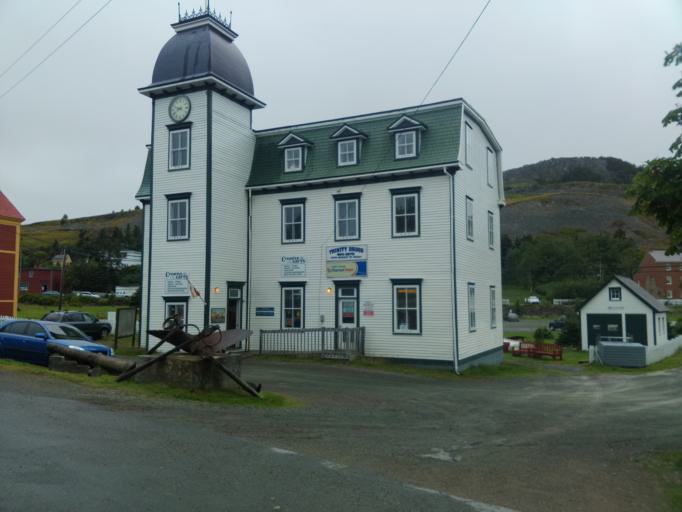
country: CA
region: Newfoundland and Labrador
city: Catalina
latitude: 48.3713
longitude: -53.3583
